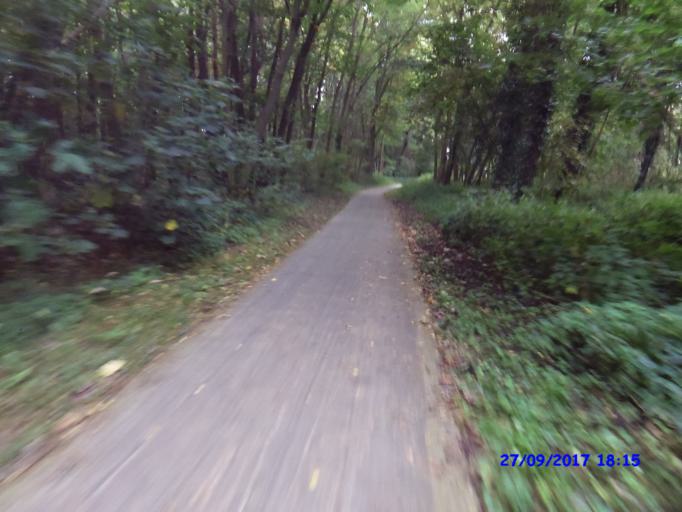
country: BE
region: Flanders
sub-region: Provincie Vlaams-Brabant
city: Aarschot
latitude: 50.9925
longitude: 4.8094
